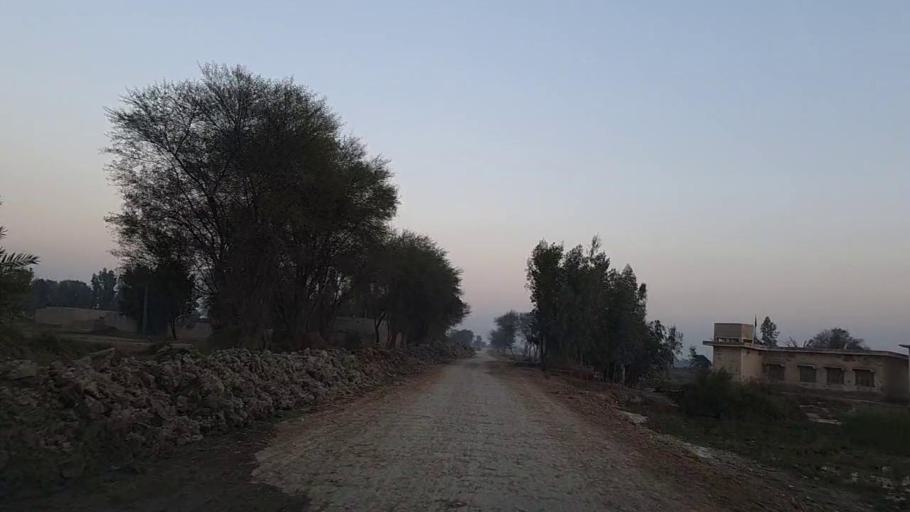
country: PK
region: Sindh
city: Naushahro Firoz
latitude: 26.7967
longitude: 68.0362
